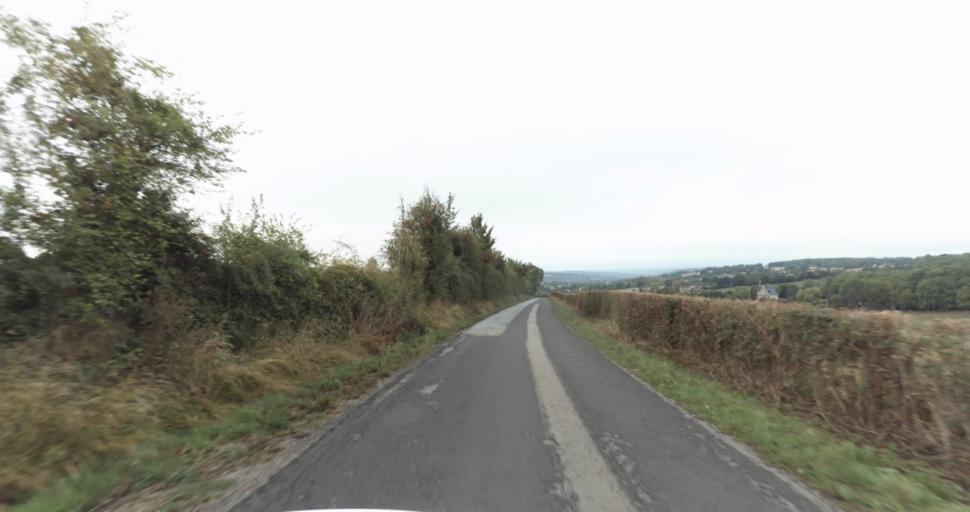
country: FR
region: Lower Normandy
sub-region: Departement de l'Orne
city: Trun
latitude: 48.9069
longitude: 0.1033
